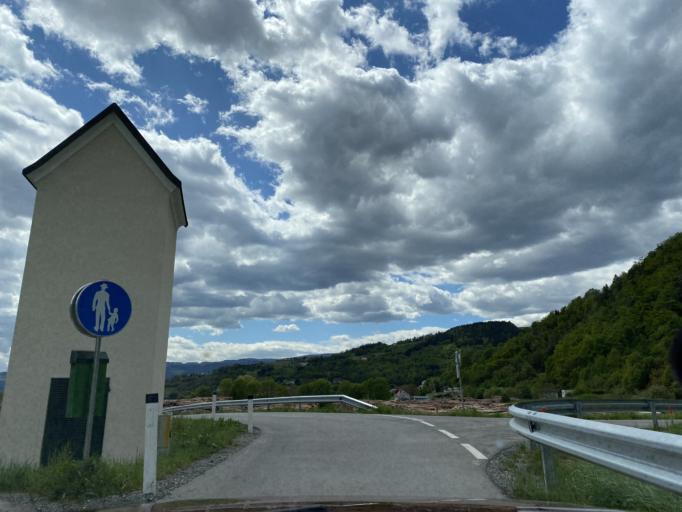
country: AT
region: Carinthia
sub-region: Politischer Bezirk Wolfsberg
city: Wolfsberg
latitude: 46.8593
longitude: 14.8523
